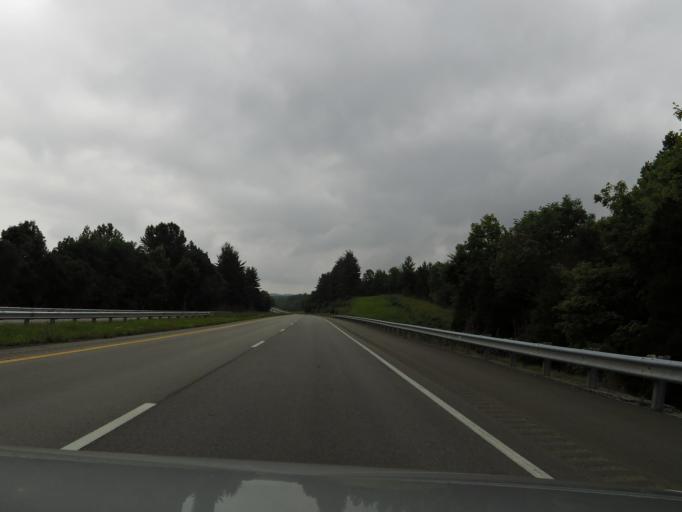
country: US
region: Kentucky
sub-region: Grayson County
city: Leitchfield
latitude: 37.4143
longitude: -86.4150
